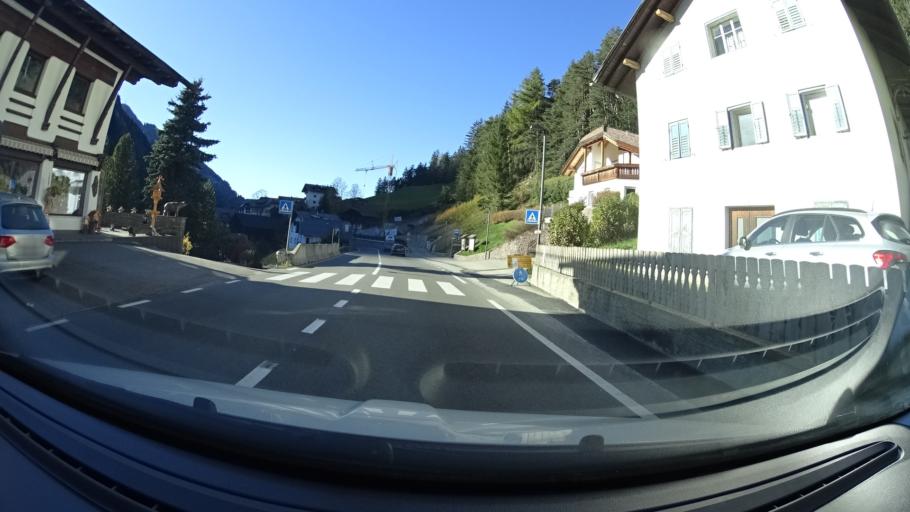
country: IT
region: Trentino-Alto Adige
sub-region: Bolzano
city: Santa Cristina Valgardena
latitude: 46.5609
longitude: 11.7075
